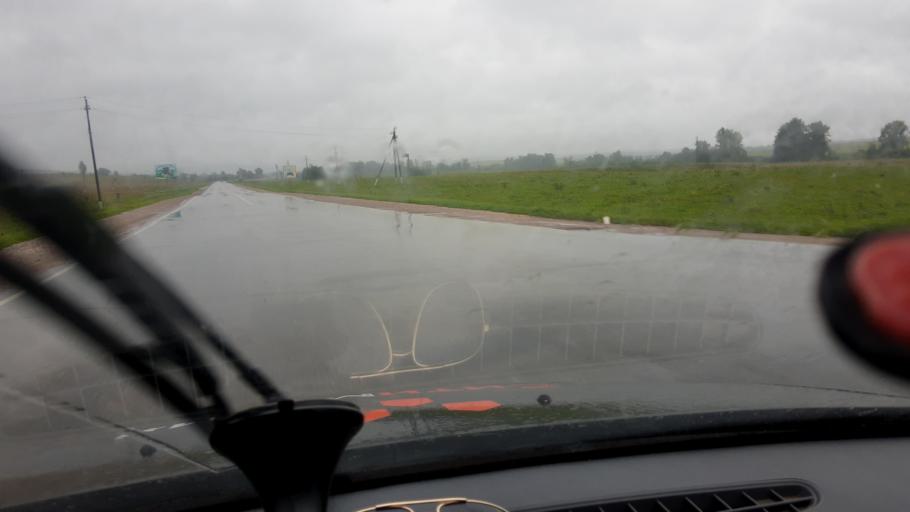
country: RU
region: Bashkortostan
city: Karmaskaly
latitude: 53.9301
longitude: 56.4215
